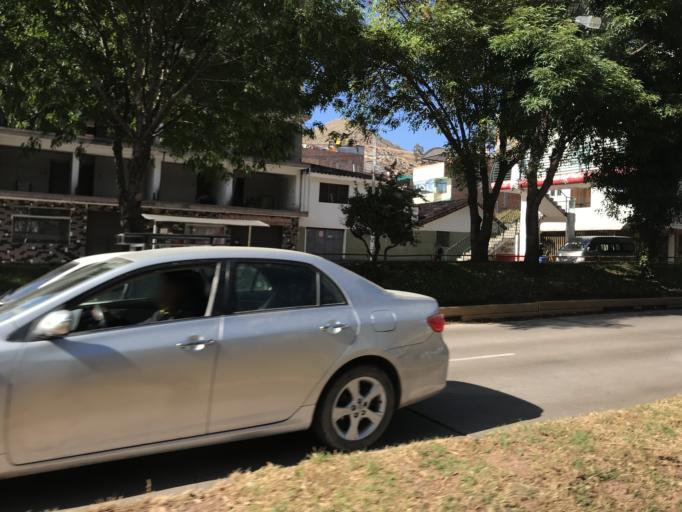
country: PE
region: Cusco
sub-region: Provincia de Cusco
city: Cusco
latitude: -13.5324
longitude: -71.9620
